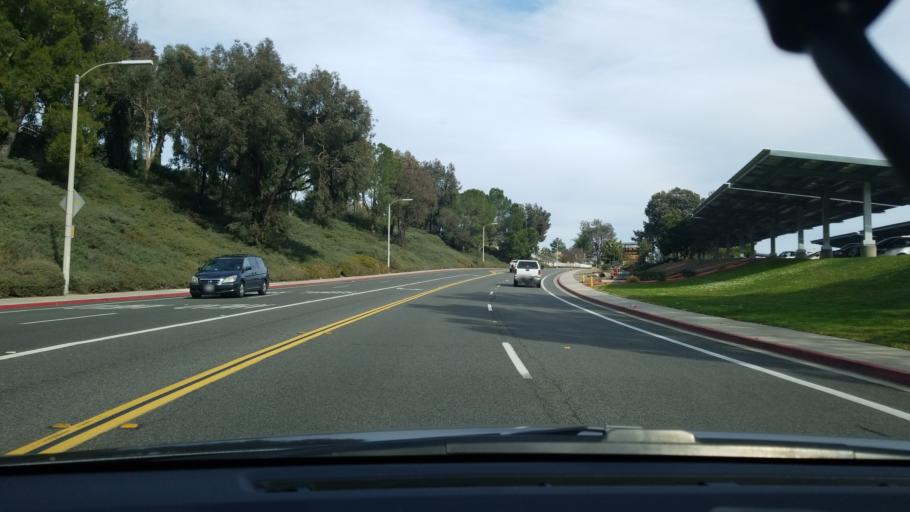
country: US
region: California
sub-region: Riverside County
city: Temecula
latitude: 33.5027
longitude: -117.1190
